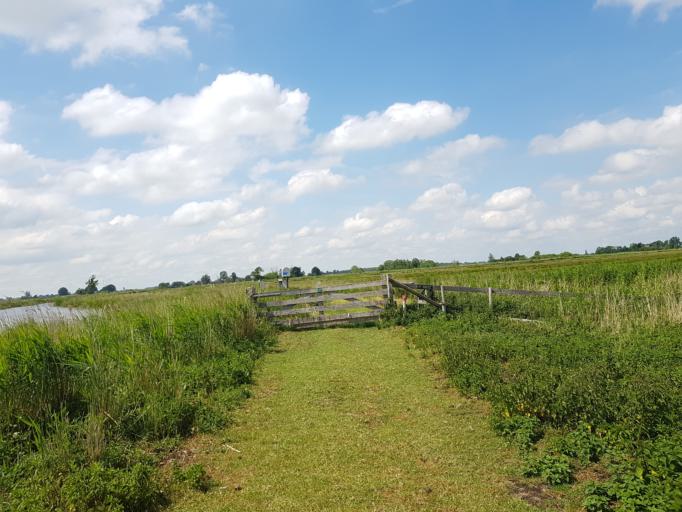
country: NL
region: Friesland
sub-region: Gemeente Boarnsterhim
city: Aldeboarn
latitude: 53.0943
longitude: 5.9006
